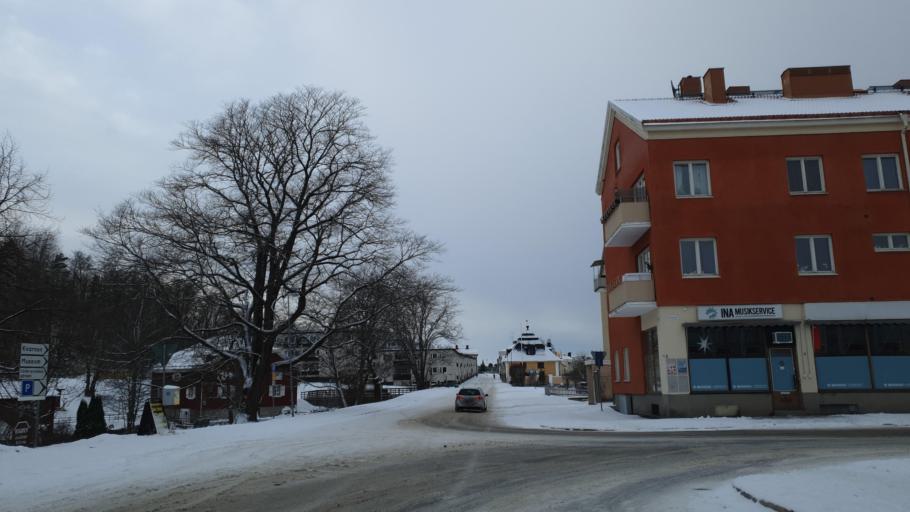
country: SE
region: Gaevleborg
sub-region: Soderhamns Kommun
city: Soderhamn
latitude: 61.3013
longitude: 17.0475
